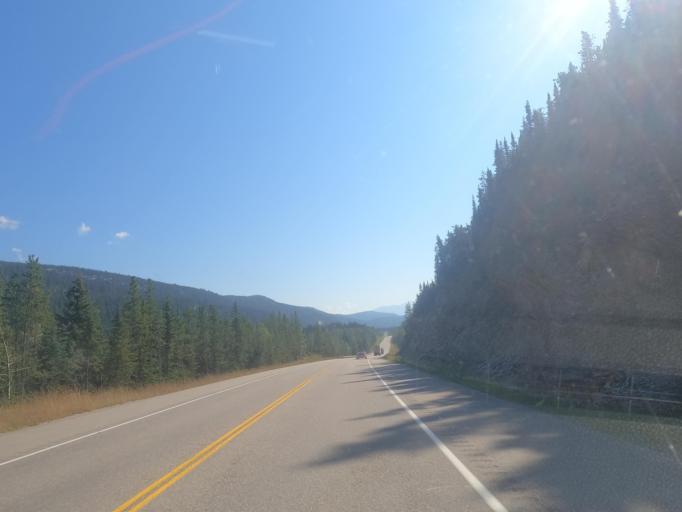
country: CA
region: Alberta
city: Jasper Park Lodge
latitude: 52.8769
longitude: -118.3330
